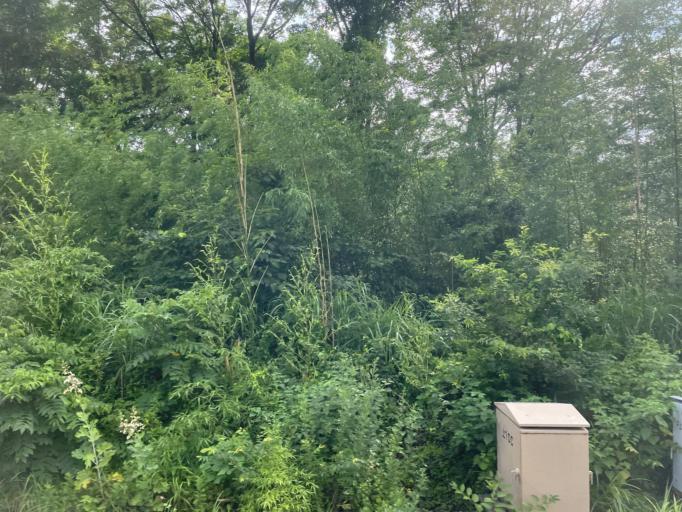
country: JP
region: Gunma
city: Numata
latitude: 36.7494
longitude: 138.9798
